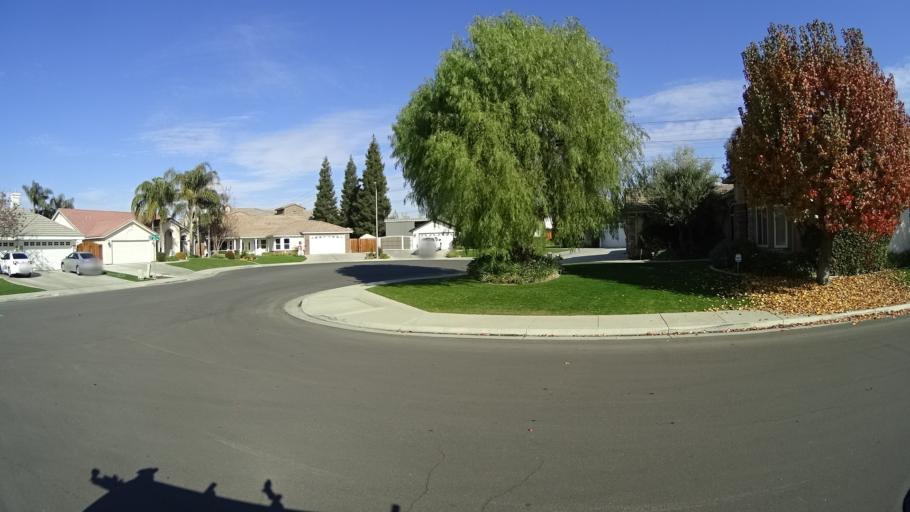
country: US
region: California
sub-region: Kern County
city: Greenacres
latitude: 35.4088
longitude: -119.0934
